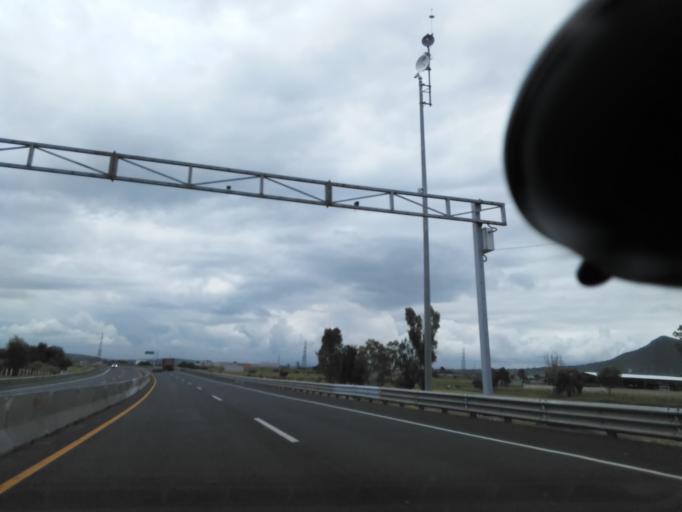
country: MX
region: Mexico
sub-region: Huehuetoca
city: Casa Nueva
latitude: 19.8240
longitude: -99.2200
